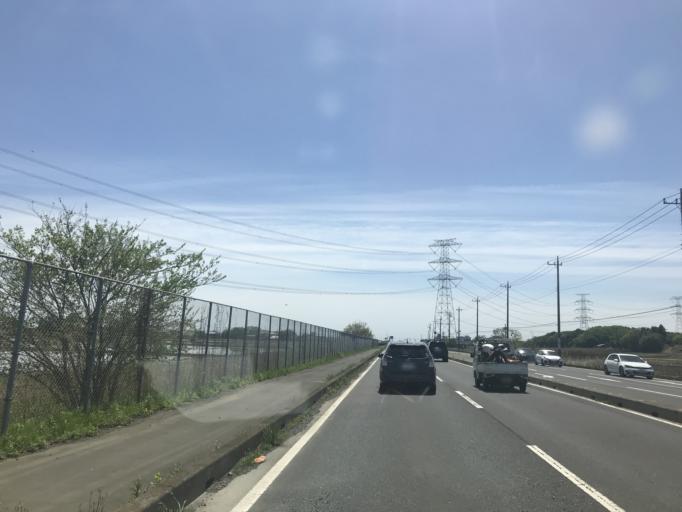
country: JP
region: Ibaraki
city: Shimodate
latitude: 36.2459
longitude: 139.9837
